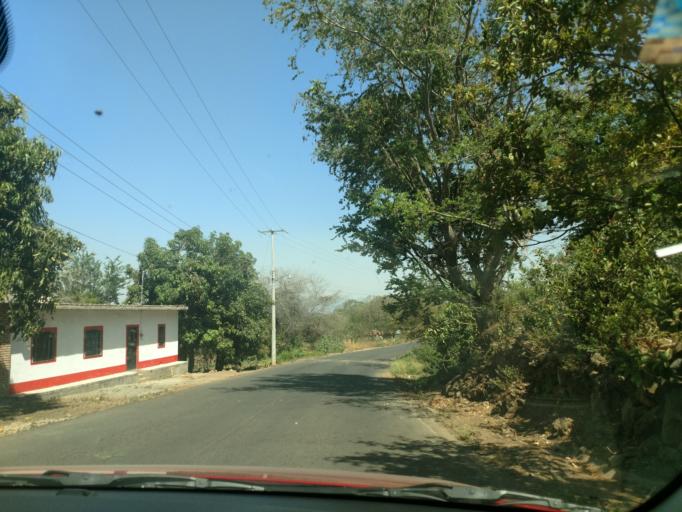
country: MX
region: Nayarit
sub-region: Tepic
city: La Corregidora
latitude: 21.4718
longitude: -104.6656
